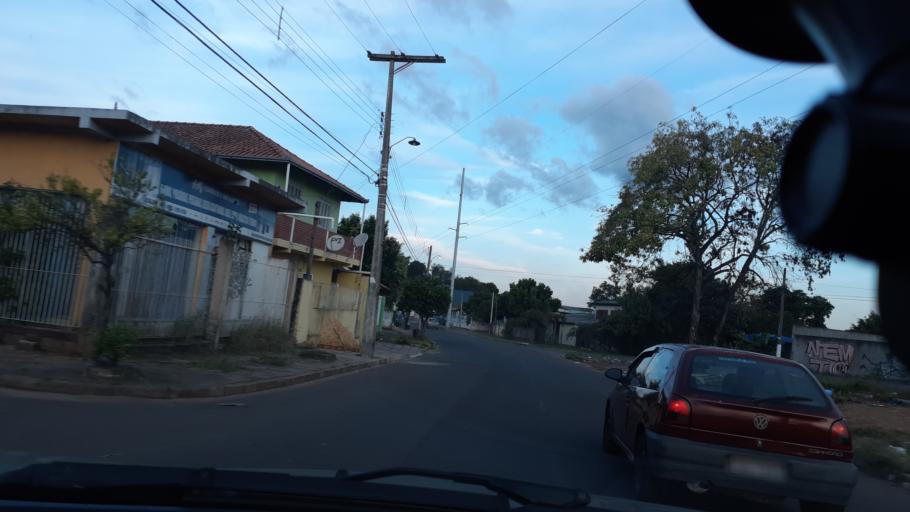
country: BR
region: Rio Grande do Sul
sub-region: Sapucaia Do Sul
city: Sapucaia
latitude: -29.8416
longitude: -51.1540
